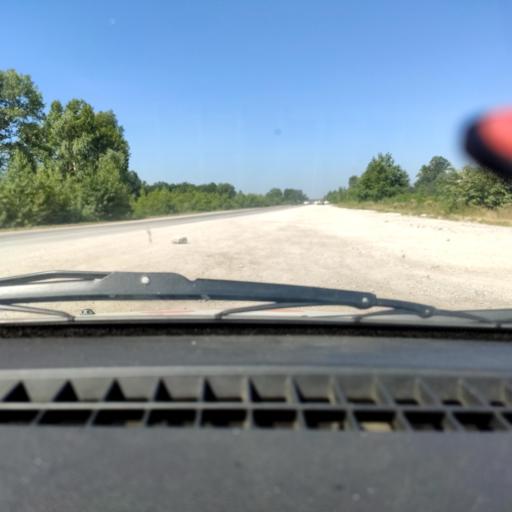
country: RU
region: Bashkortostan
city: Sterlitamak
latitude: 53.6400
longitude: 56.0645
